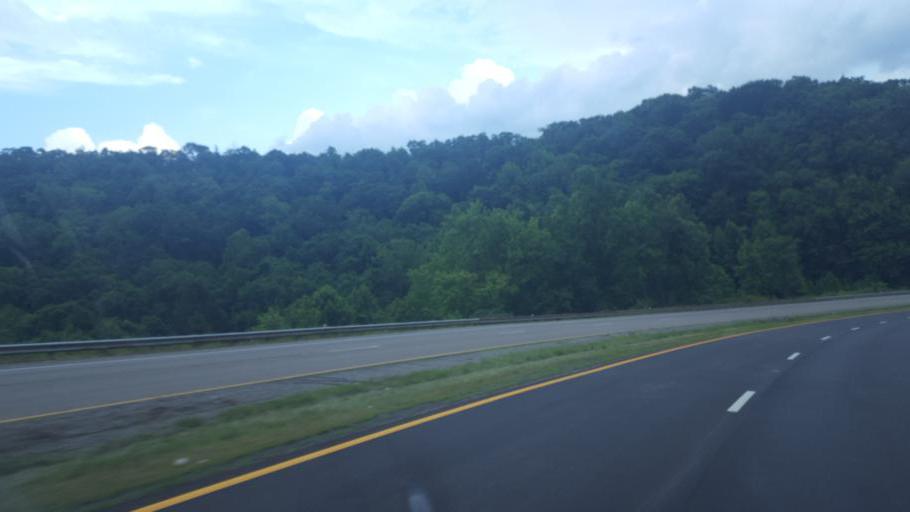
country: US
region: Kentucky
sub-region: Letcher County
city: Jenkins
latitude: 37.1558
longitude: -82.6155
